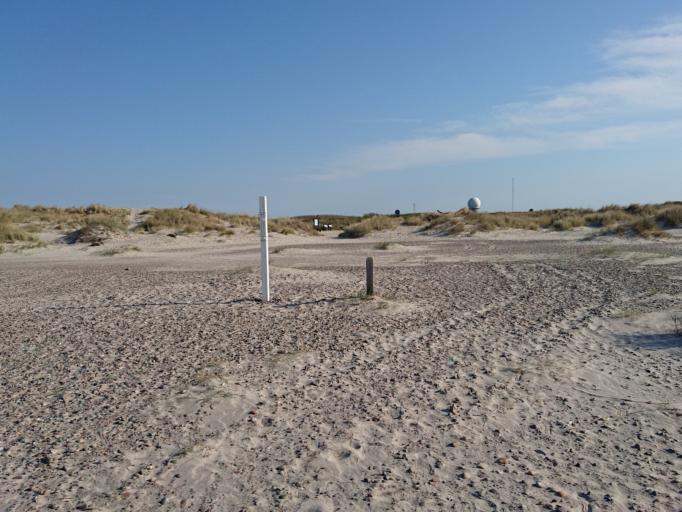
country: DK
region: North Denmark
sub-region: Frederikshavn Kommune
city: Skagen
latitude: 57.7512
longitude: 10.6042
